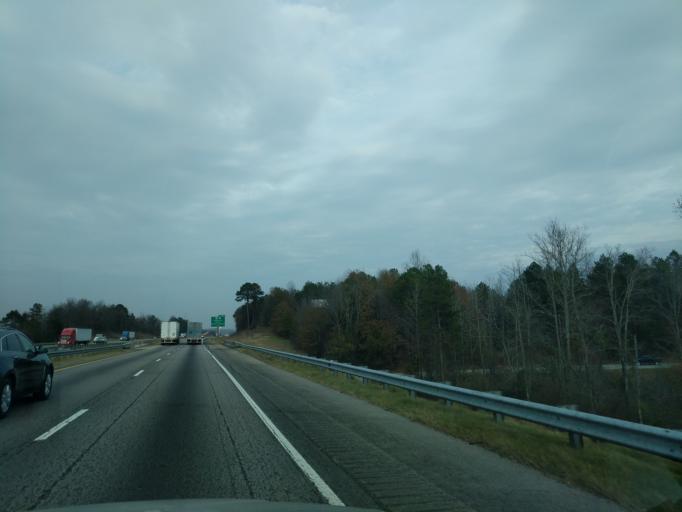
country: US
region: Georgia
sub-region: Jackson County
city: Commerce
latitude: 34.2414
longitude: -83.4840
